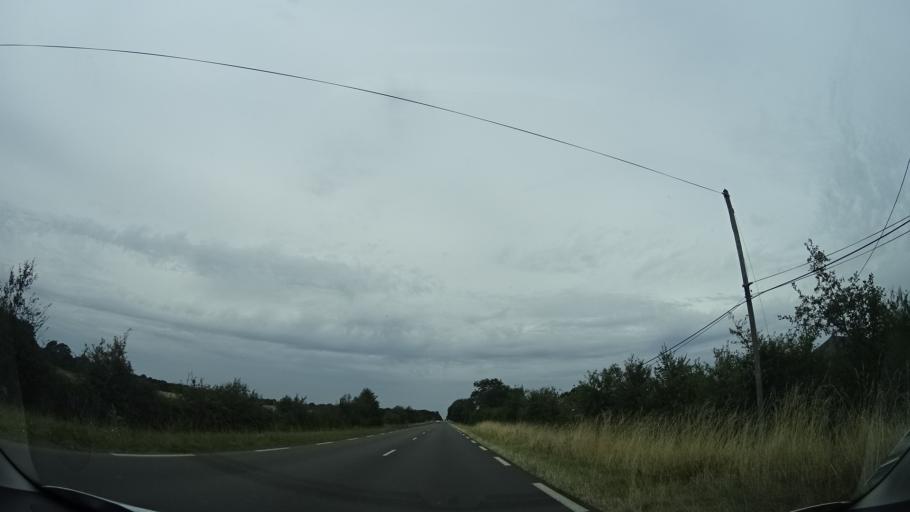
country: FR
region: Pays de la Loire
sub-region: Departement de la Mayenne
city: Meslay-du-Maine
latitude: 47.9778
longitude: -0.6043
